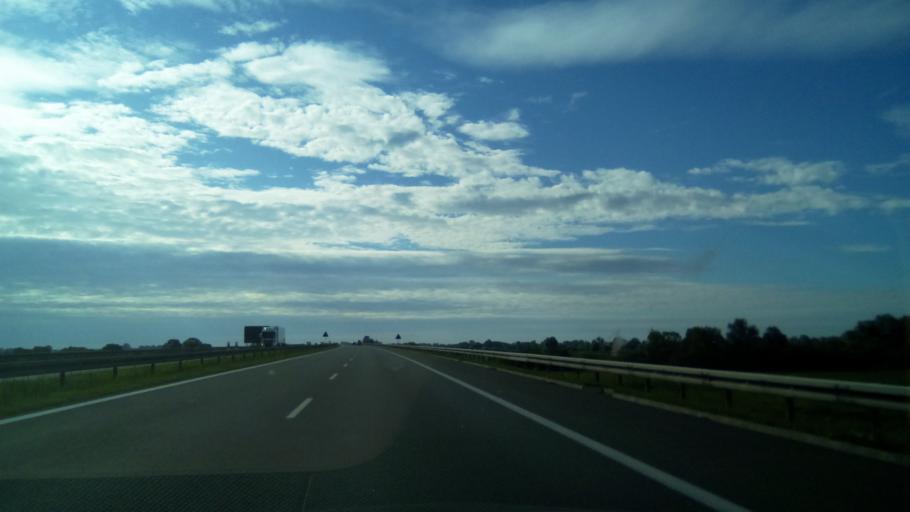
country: PL
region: Greater Poland Voivodeship
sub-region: Powiat koninski
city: Rzgow Pierwszy
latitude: 52.1982
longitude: 18.0421
